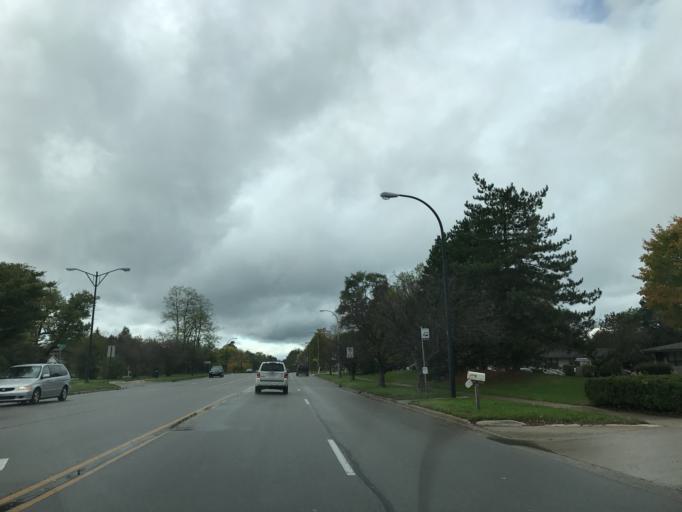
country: US
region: Michigan
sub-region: Washtenaw County
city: Ann Arbor
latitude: 42.2451
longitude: -83.7005
